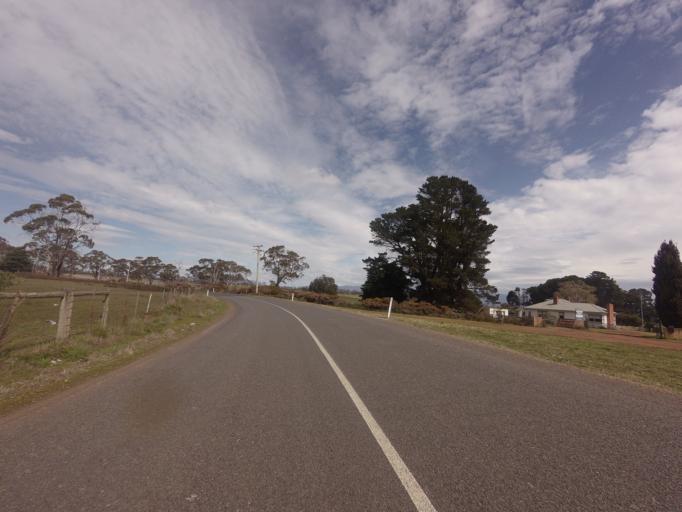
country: AU
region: Tasmania
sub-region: Northern Midlands
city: Longford
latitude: -41.7174
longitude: 147.1869
